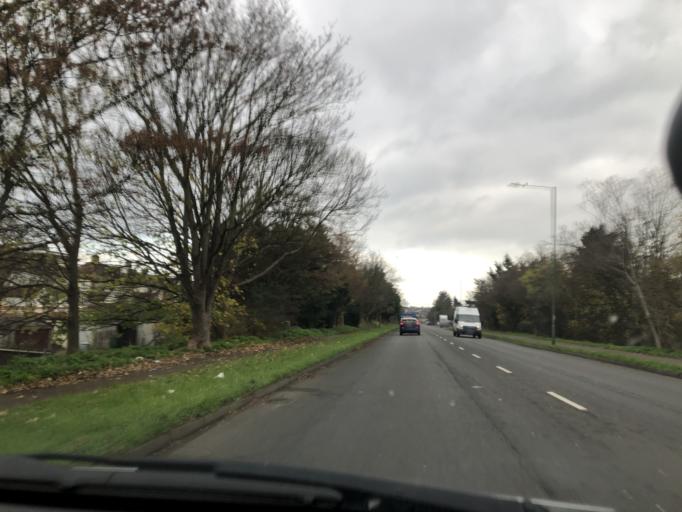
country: GB
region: England
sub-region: Kent
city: Dartford
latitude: 51.4457
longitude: 0.1922
